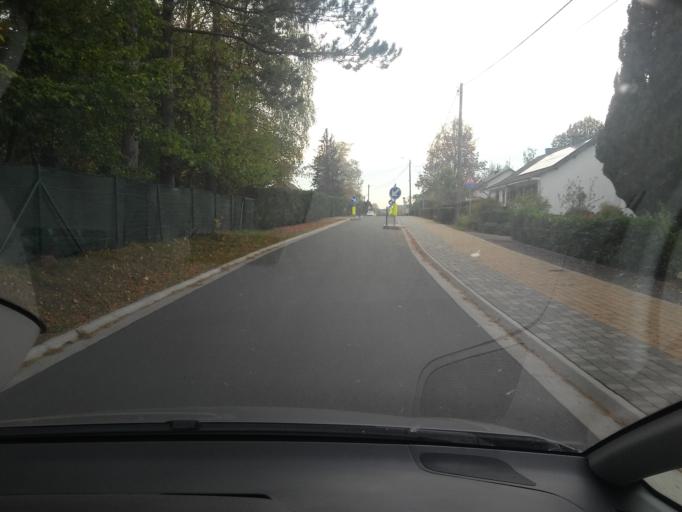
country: BE
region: Wallonia
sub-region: Province du Luxembourg
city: Arlon
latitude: 49.6989
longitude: 5.8186
